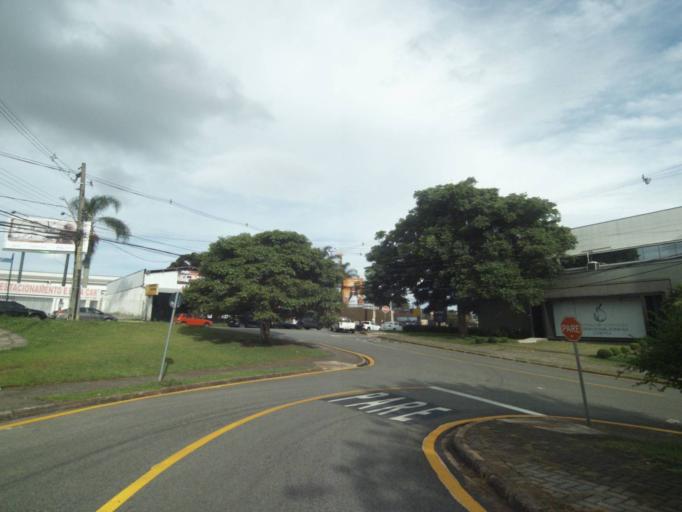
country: BR
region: Parana
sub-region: Curitiba
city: Curitiba
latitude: -25.4413
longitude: -49.3086
